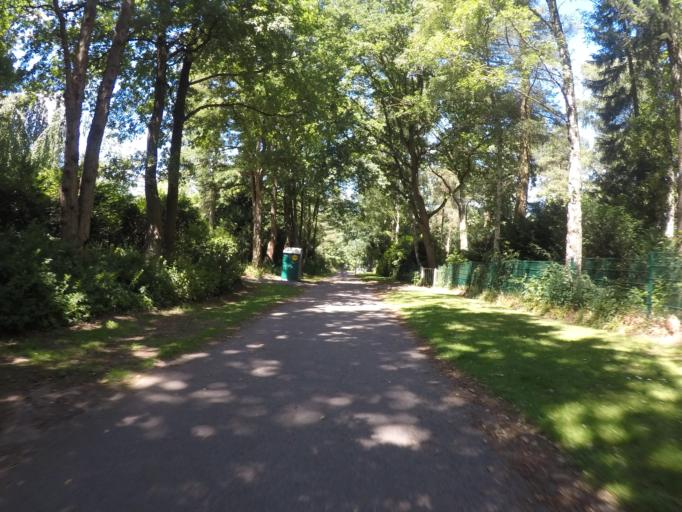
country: DE
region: Schleswig-Holstein
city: Halstenbek
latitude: 53.5742
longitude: 9.7999
